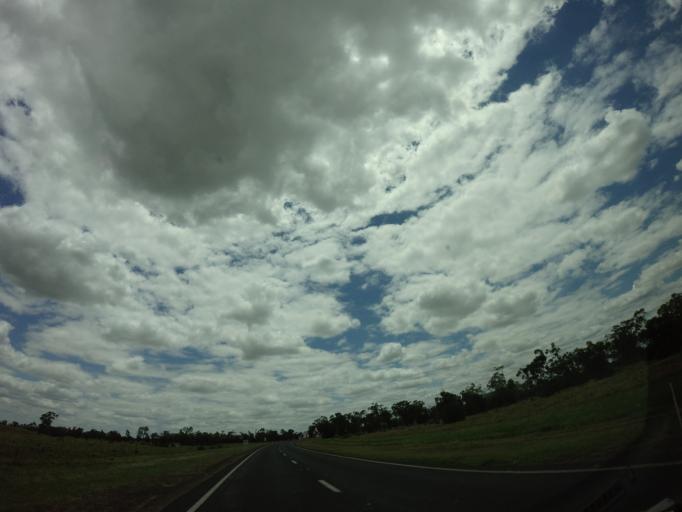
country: AU
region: New South Wales
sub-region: Moree Plains
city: Boggabilla
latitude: -28.6137
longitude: 150.3481
